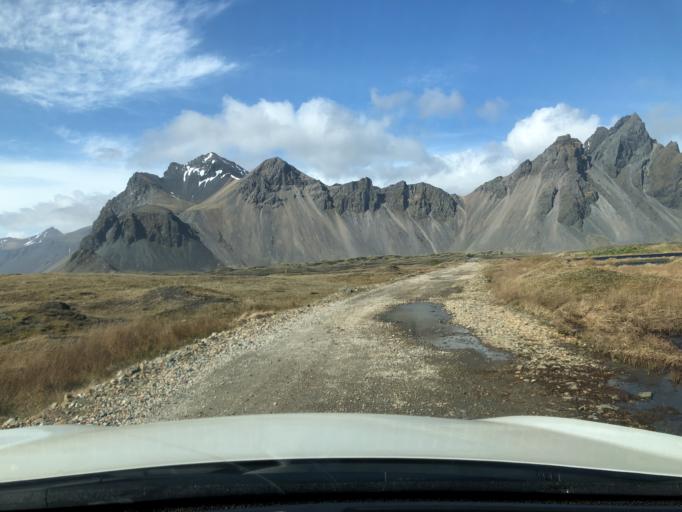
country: IS
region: East
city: Hoefn
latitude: 64.2413
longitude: -14.9718
